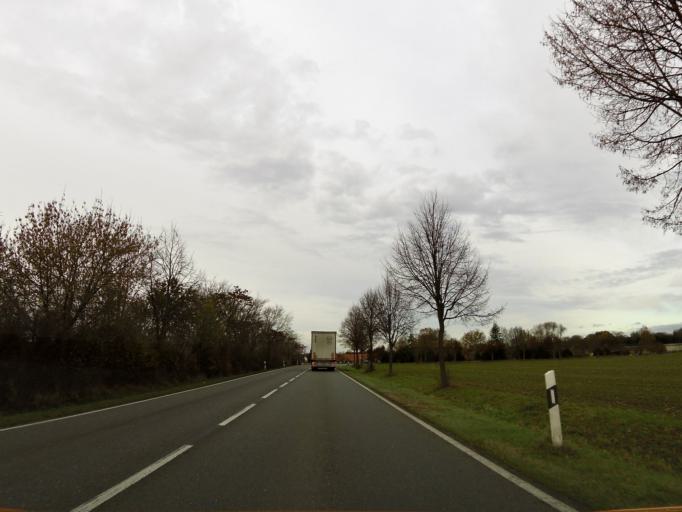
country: DE
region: Saxony-Anhalt
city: Pretzier
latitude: 52.7878
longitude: 11.2321
